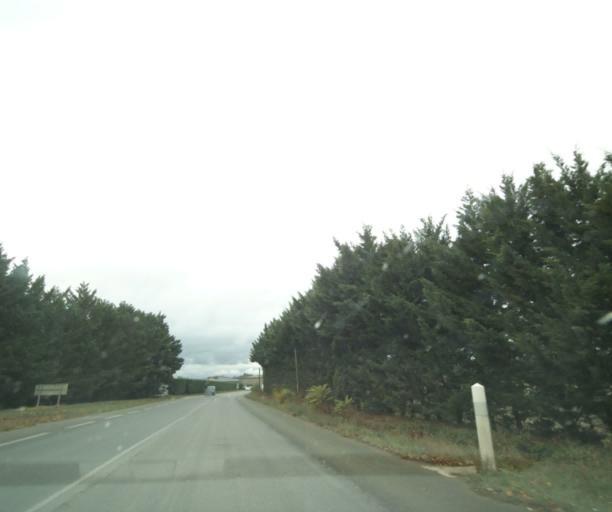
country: FR
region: Auvergne
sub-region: Departement du Puy-de-Dome
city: Pont-du-Chateau
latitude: 45.8164
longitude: 3.2633
